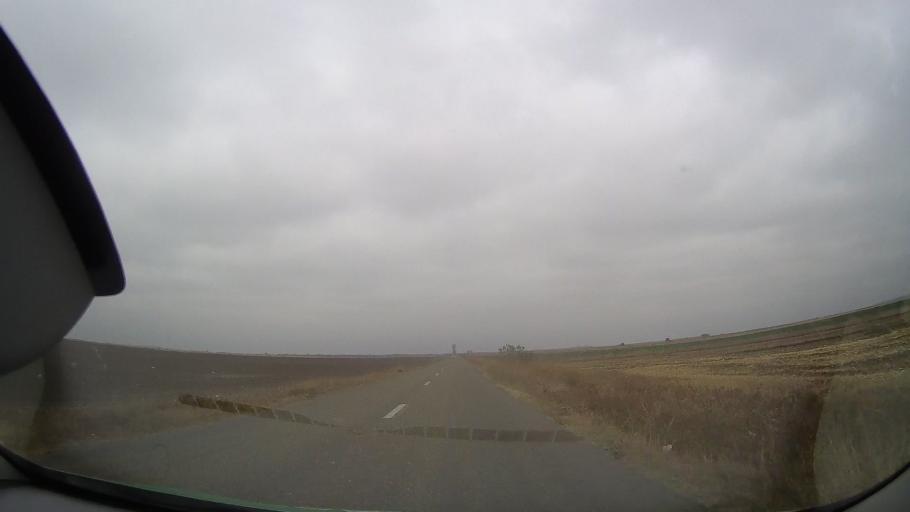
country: RO
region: Buzau
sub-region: Comuna Bradeanu
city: Bradeanu
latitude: 44.8976
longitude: 26.8728
